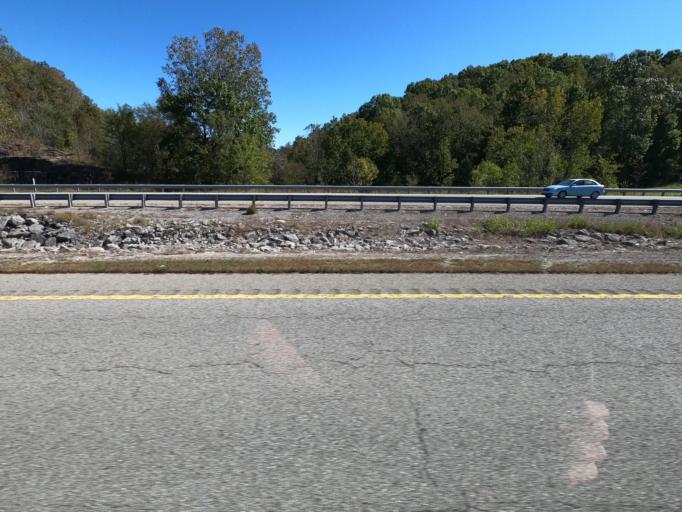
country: US
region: Tennessee
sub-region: Maury County
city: Mount Pleasant
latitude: 35.4695
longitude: -87.2651
